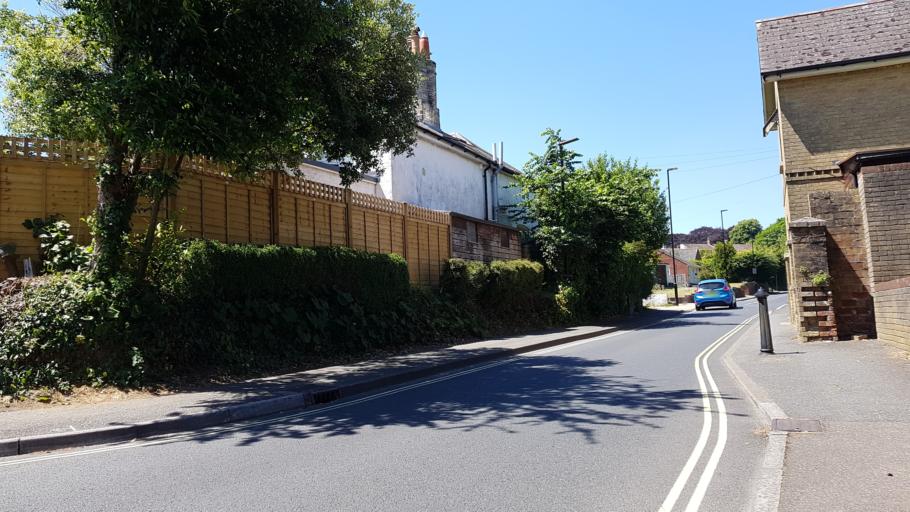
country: GB
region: England
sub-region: Isle of Wight
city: Newport
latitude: 50.6913
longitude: -1.2899
